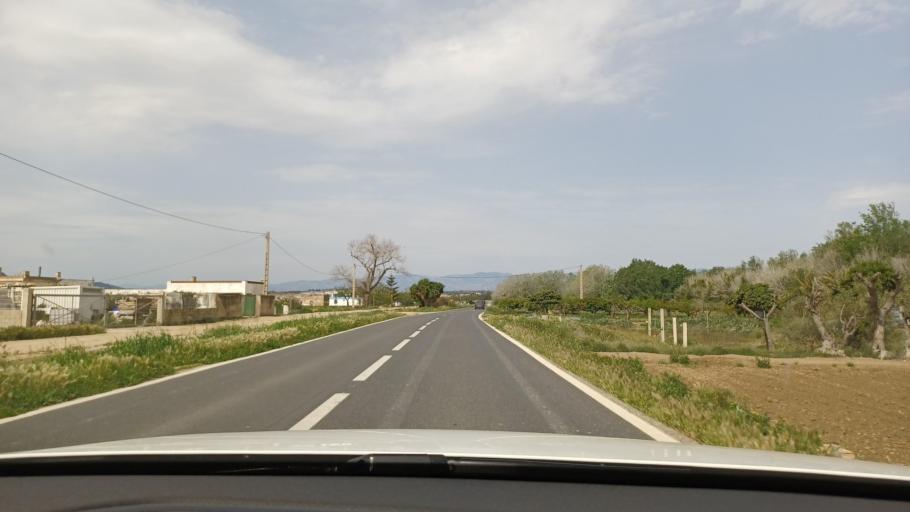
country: ES
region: Catalonia
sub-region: Provincia de Tarragona
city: Amposta
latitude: 40.7043
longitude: 0.6055
